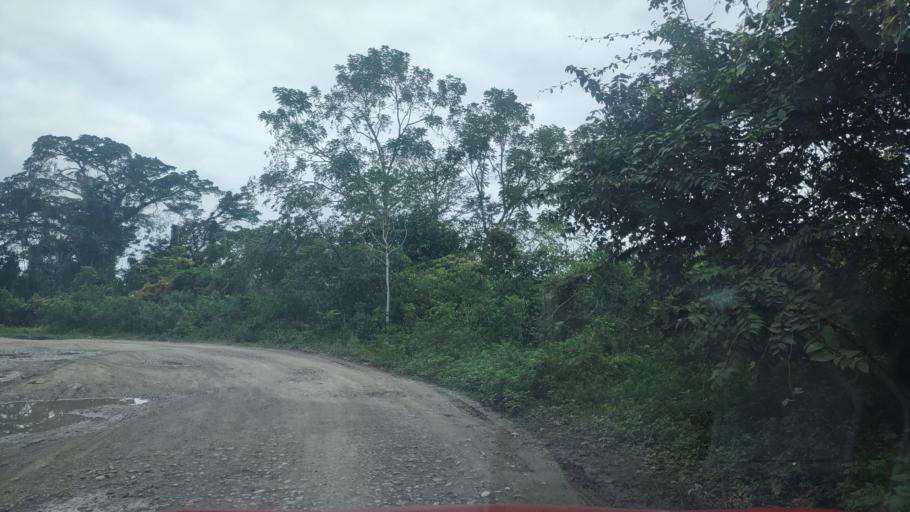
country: MX
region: Veracruz
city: Papantla de Olarte
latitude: 20.4212
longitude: -97.2674
